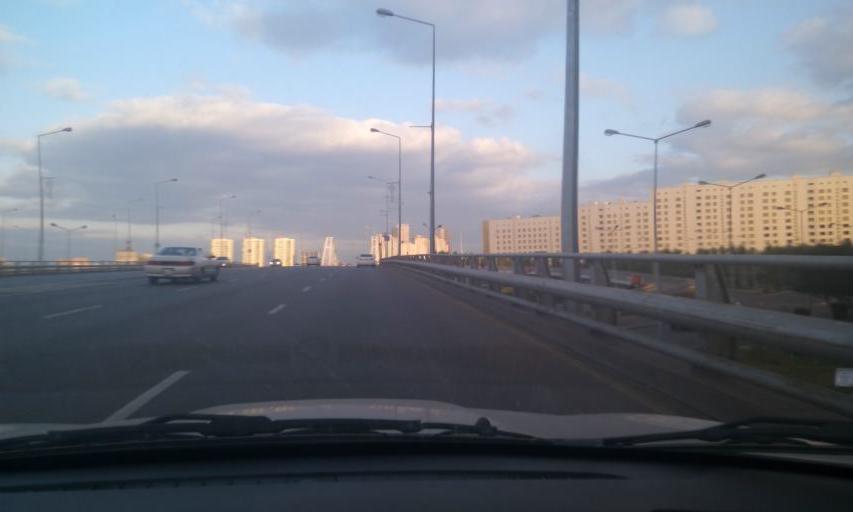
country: KZ
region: Astana Qalasy
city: Astana
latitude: 51.1326
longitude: 71.4380
